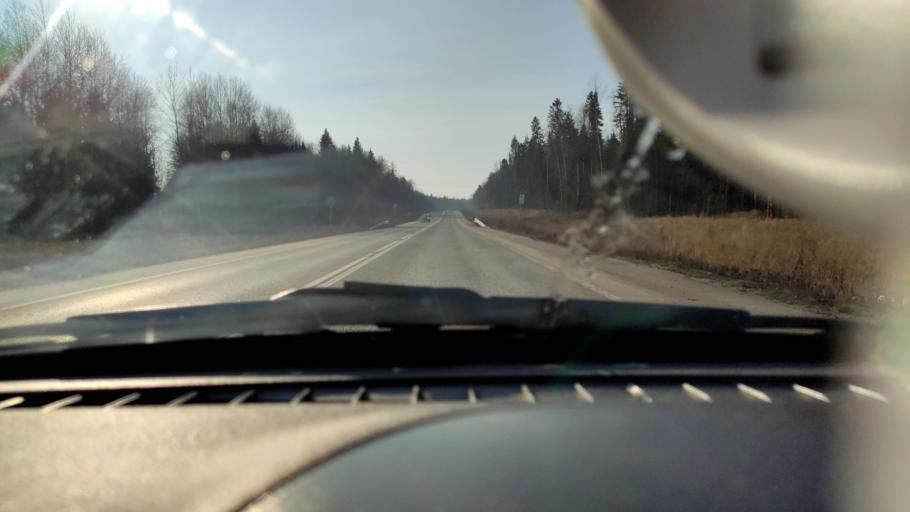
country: RU
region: Perm
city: Novyye Lyady
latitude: 58.0438
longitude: 56.5433
